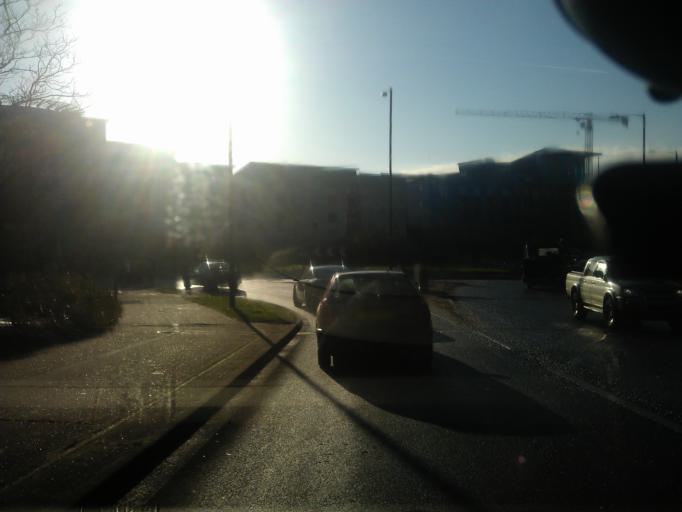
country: GB
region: England
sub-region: Essex
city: Rowhedge
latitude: 51.8811
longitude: 0.9313
